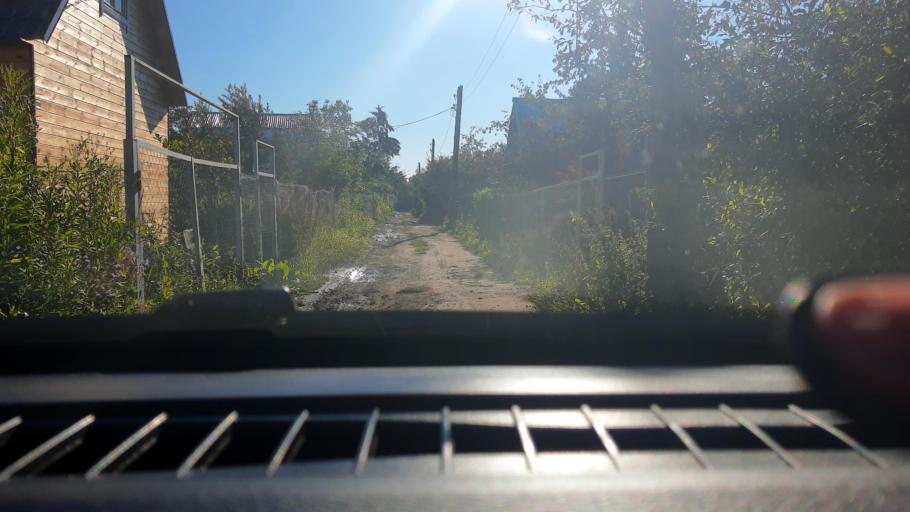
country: RU
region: Nizjnij Novgorod
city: Gorbatovka
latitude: 56.3147
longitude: 43.8276
